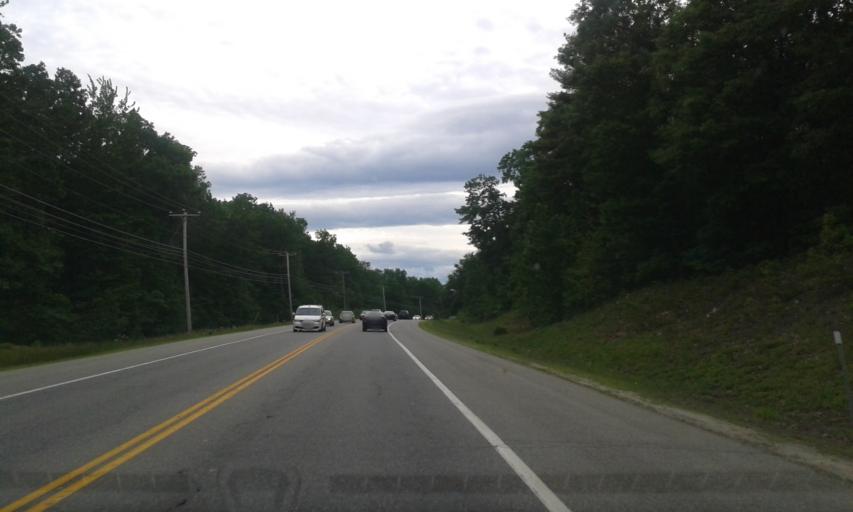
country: US
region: New Hampshire
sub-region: Hillsborough County
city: Litchfield
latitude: 42.8082
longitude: -71.5279
